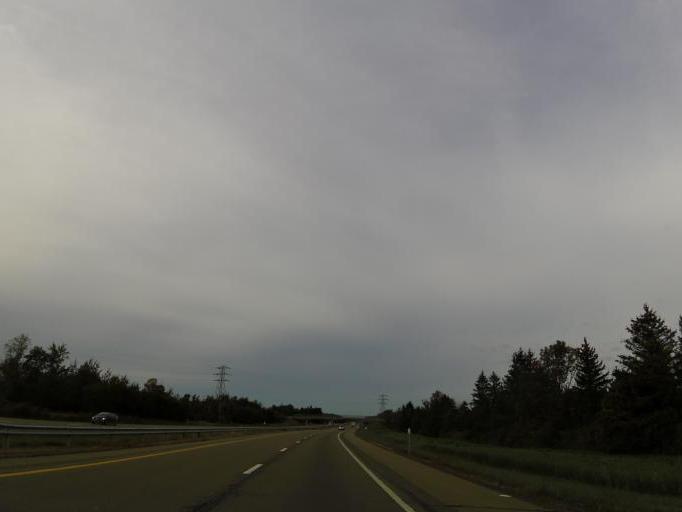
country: US
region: New York
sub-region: Chautauqua County
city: Dunkirk
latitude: 42.4809
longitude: -79.2620
